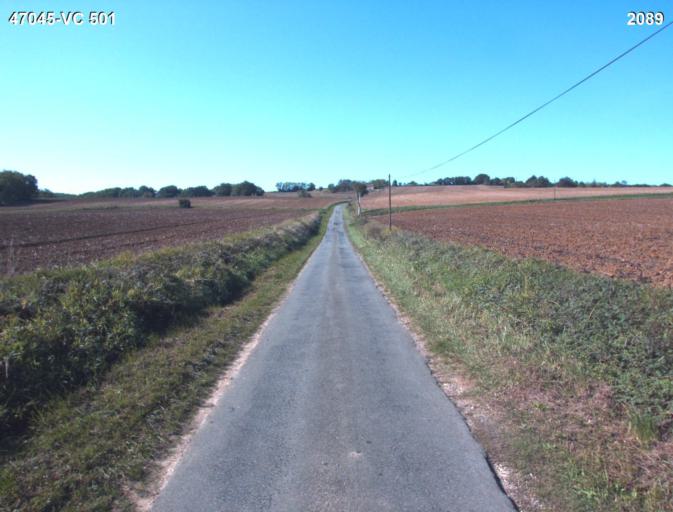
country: FR
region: Aquitaine
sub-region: Departement du Lot-et-Garonne
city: Nerac
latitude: 44.1654
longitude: 0.4190
